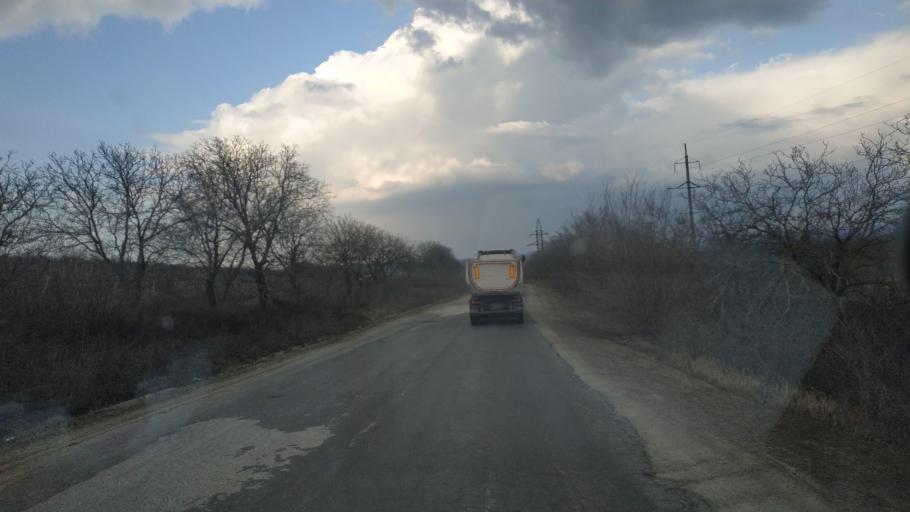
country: MD
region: Anenii Noi
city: Anenii Noi
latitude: 46.9682
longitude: 29.2847
